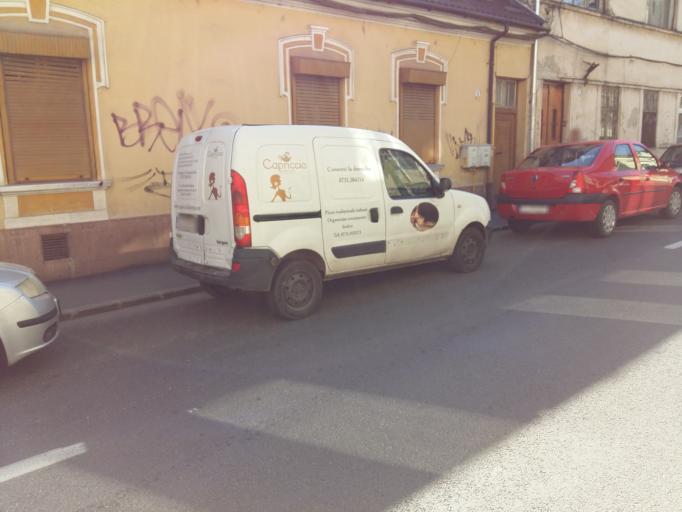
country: RO
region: Cluj
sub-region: Municipiul Cluj-Napoca
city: Cluj-Napoca
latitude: 46.7665
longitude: 23.5815
